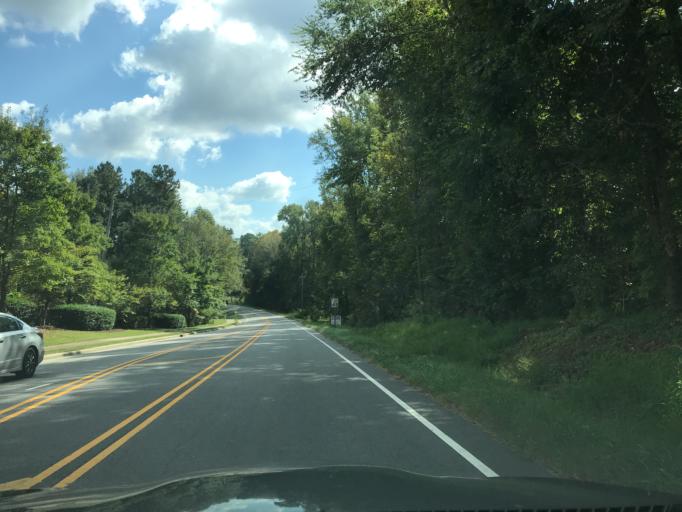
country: US
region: North Carolina
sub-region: Wake County
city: Wake Forest
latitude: 35.9316
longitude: -78.5289
